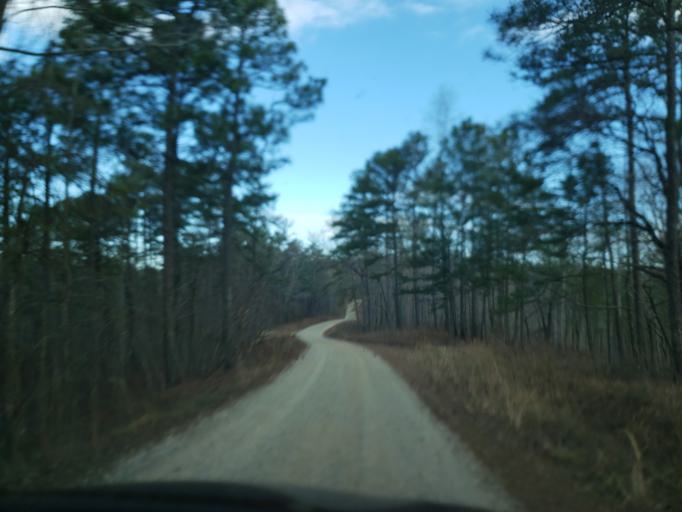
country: US
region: Alabama
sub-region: Cleburne County
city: Heflin
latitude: 33.6644
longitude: -85.6315
